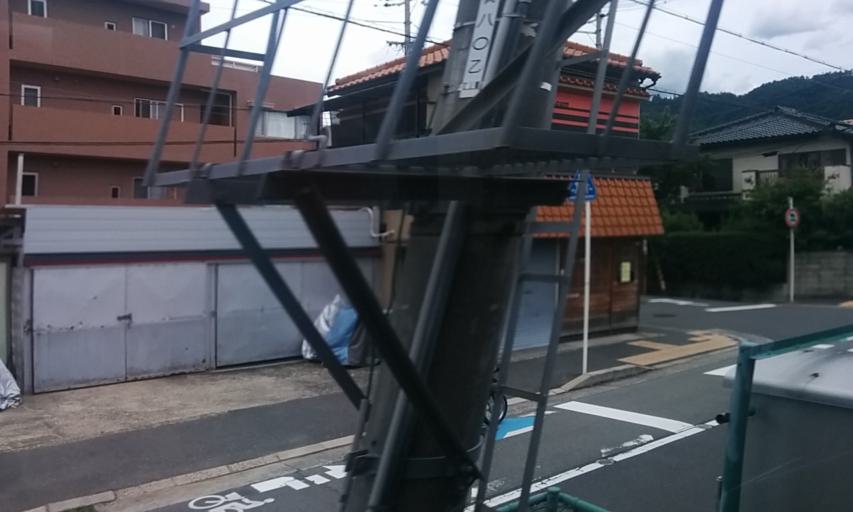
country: JP
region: Osaka
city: Mino
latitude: 34.8287
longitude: 135.4669
